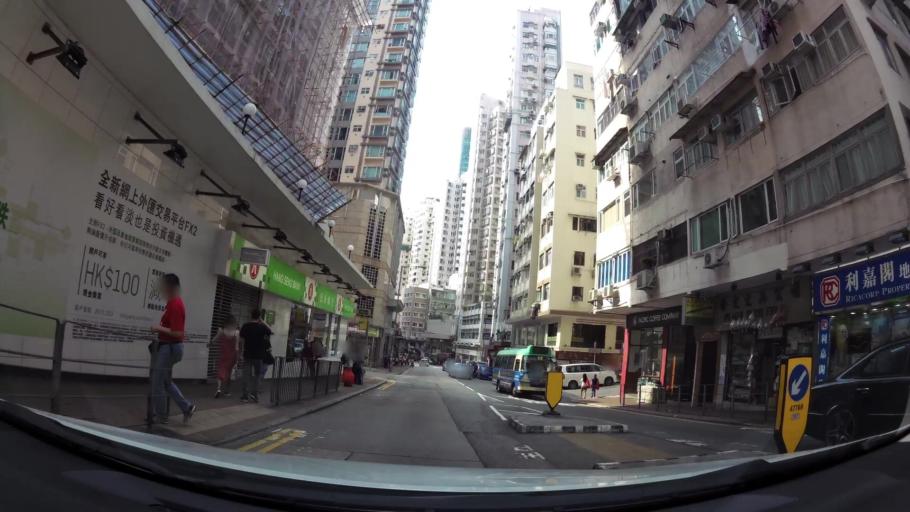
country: HK
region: Wanchai
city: Wan Chai
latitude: 22.2679
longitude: 114.1867
